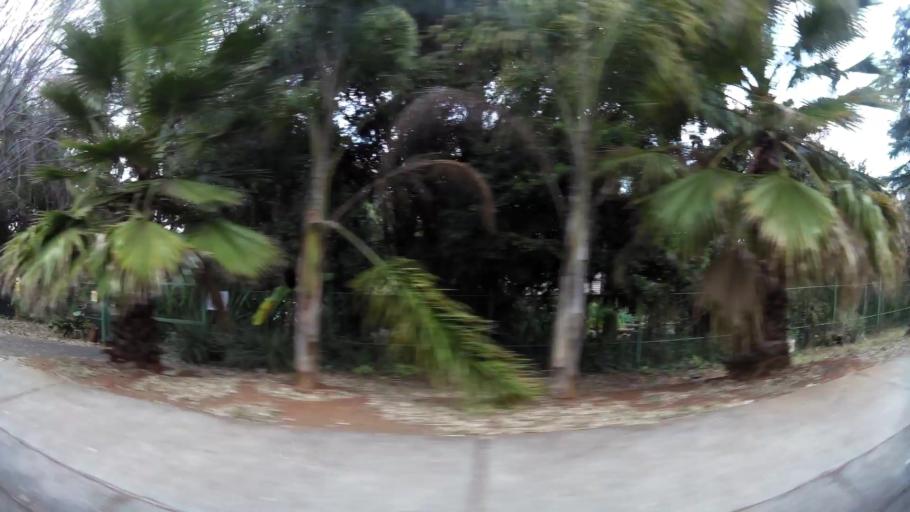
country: ZA
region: Gauteng
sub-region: City of Tshwane Metropolitan Municipality
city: Pretoria
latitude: -25.7629
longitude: 28.2822
